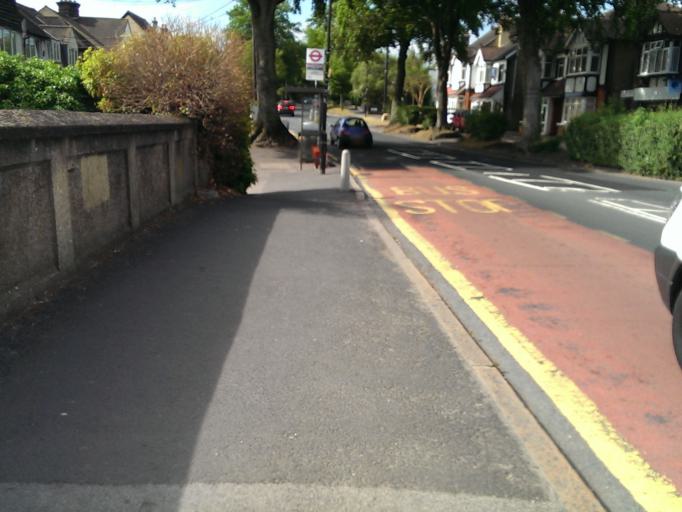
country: GB
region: England
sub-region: Greater London
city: Carshalton
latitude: 51.3572
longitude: -0.1702
